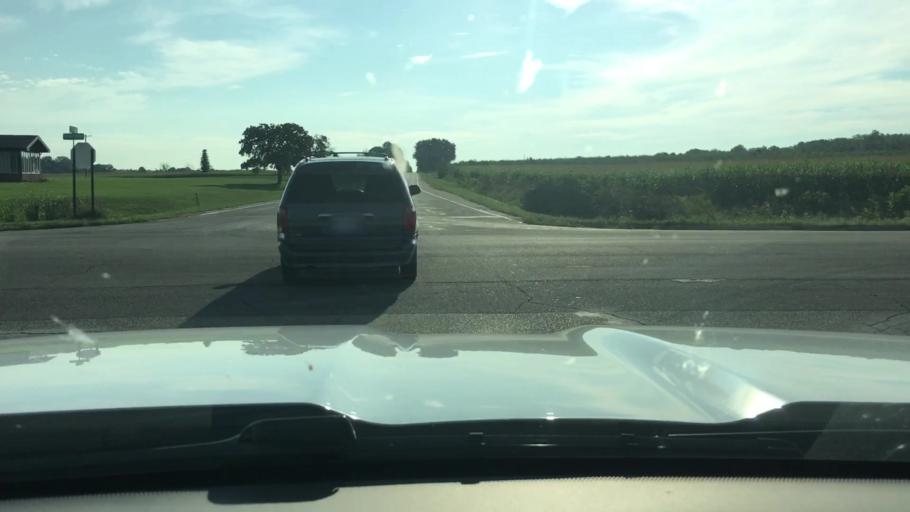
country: US
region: Michigan
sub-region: Kent County
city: Kent City
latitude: 43.1909
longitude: -85.7710
